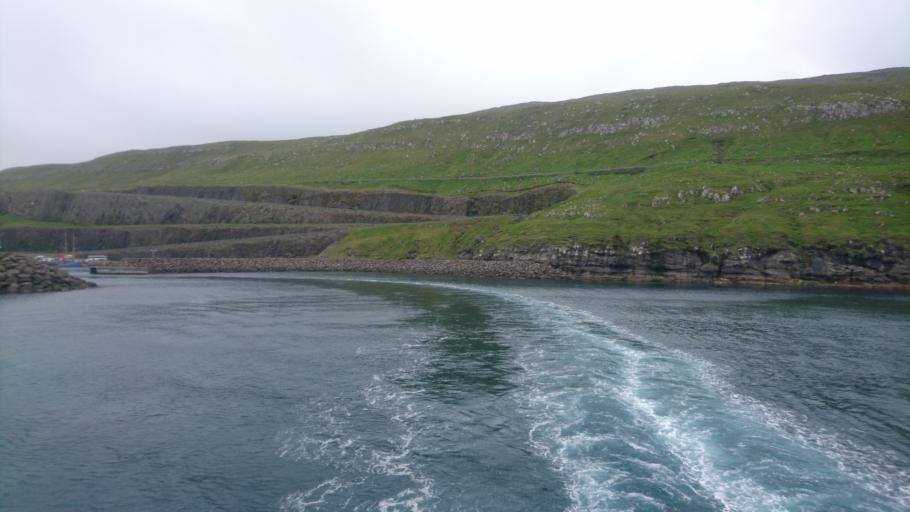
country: FO
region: Streymoy
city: Argir
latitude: 61.9585
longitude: -6.8169
